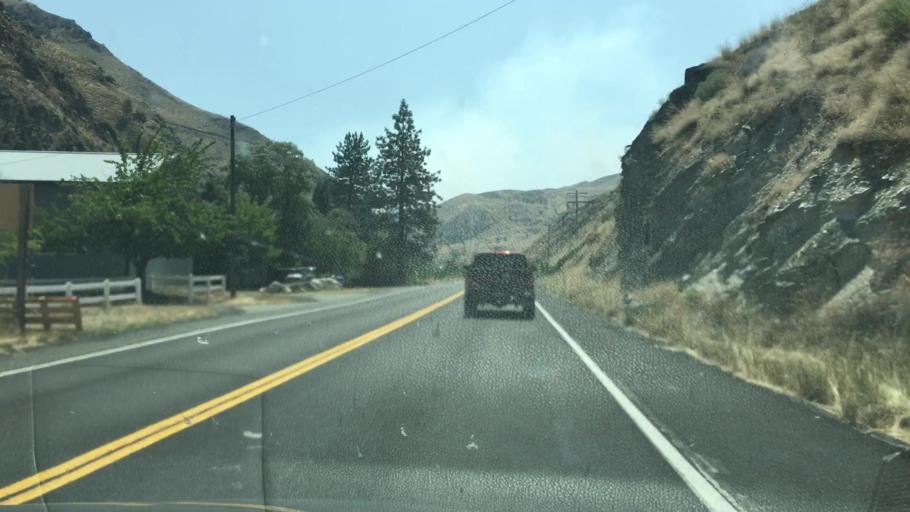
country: US
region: Idaho
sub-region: Valley County
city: McCall
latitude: 45.3691
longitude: -116.3589
